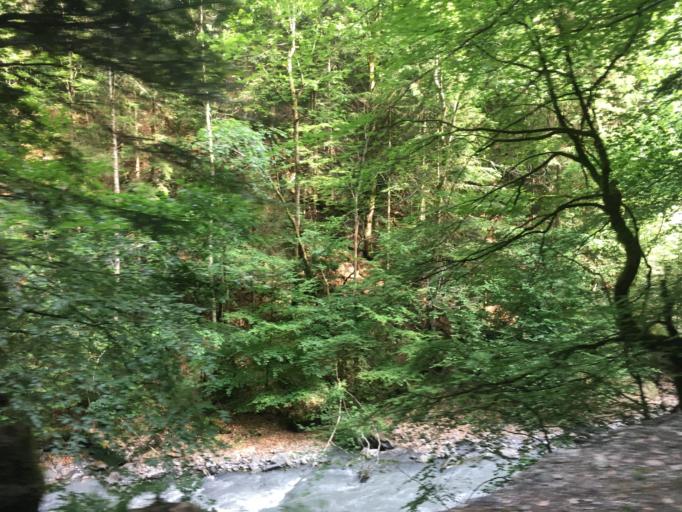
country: CH
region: Saint Gallen
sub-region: Wahlkreis Sarganserland
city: Bad Ragaz
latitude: 46.9847
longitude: 9.4916
